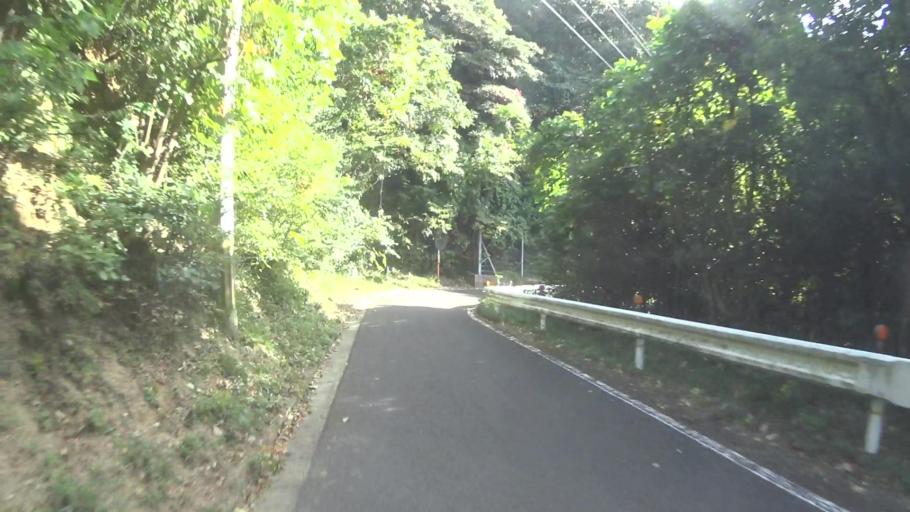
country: JP
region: Kyoto
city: Maizuru
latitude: 35.5646
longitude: 135.4093
